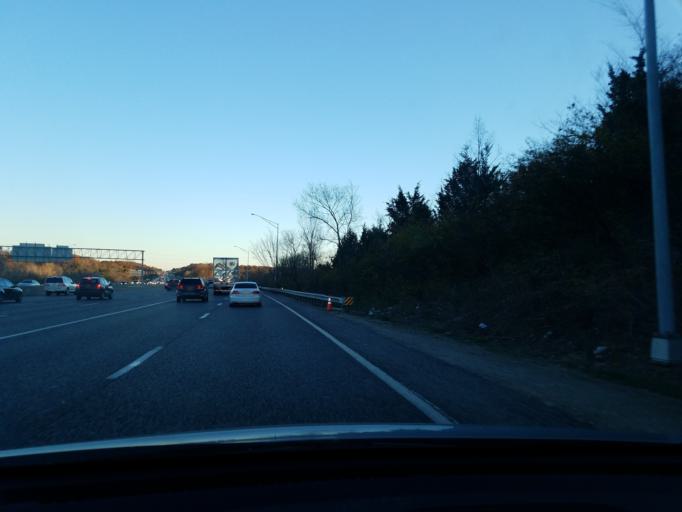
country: US
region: Missouri
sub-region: Saint Louis County
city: Sunset Hills
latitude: 38.5442
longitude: -90.4233
